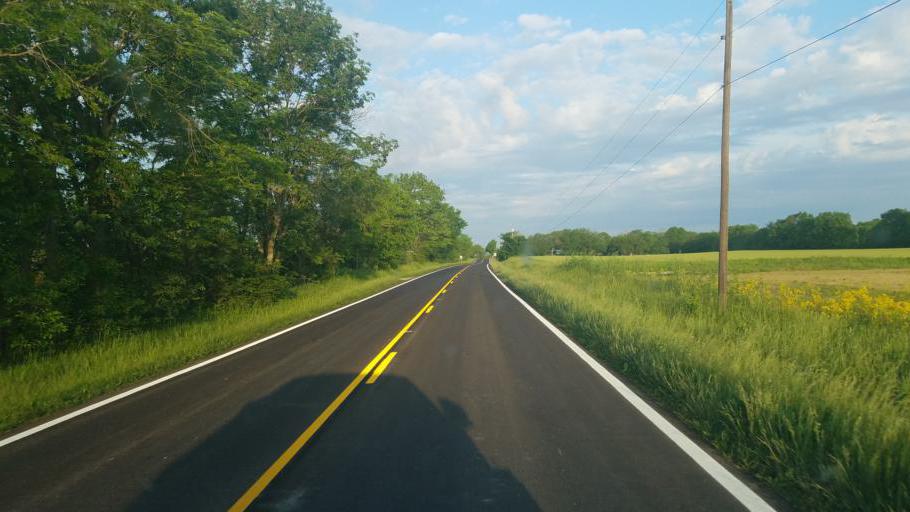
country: US
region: Ohio
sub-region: Highland County
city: Leesburg
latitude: 39.3554
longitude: -83.5327
